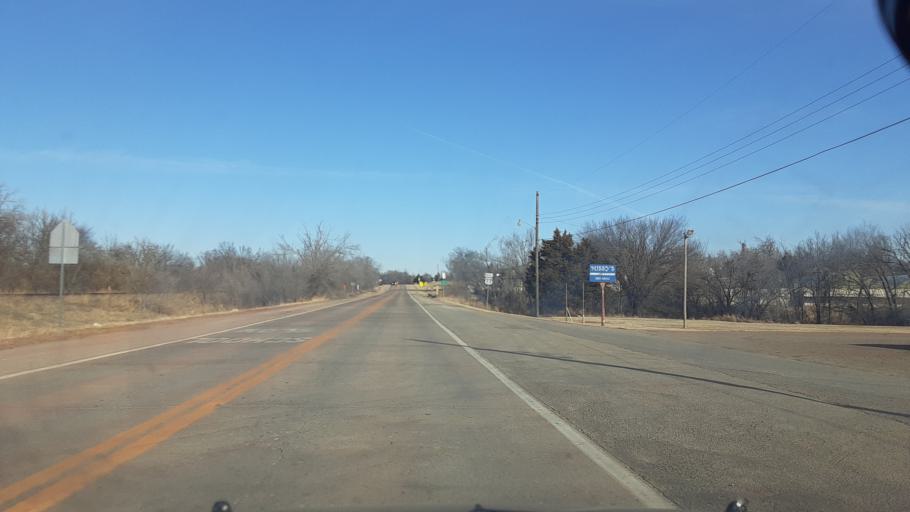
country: US
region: Oklahoma
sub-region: Logan County
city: Guthrie
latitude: 35.8886
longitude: -97.4240
